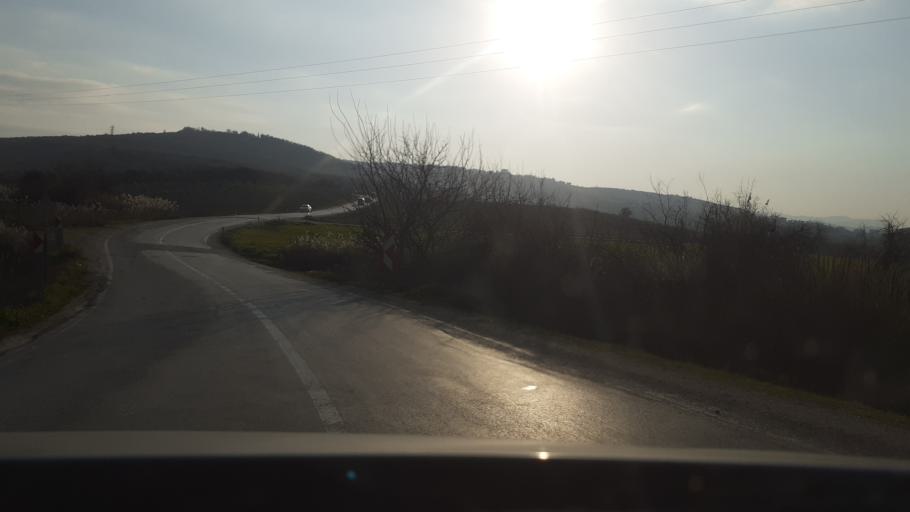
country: TR
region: Hatay
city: Oymakli
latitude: 36.1139
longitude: 36.2810
